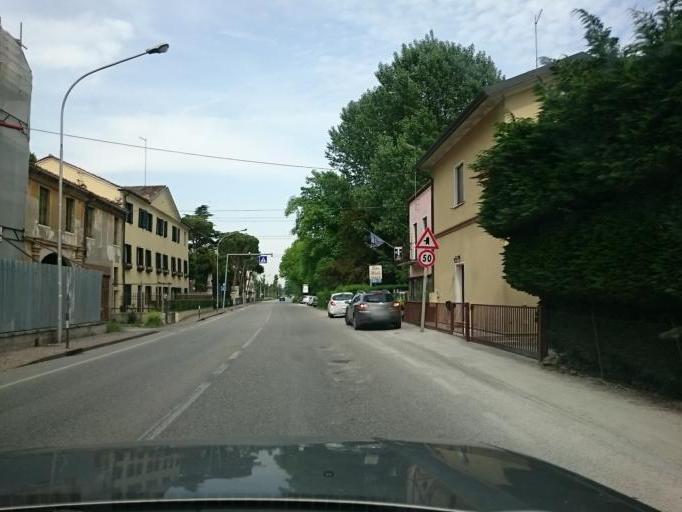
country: IT
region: Veneto
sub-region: Provincia di Venezia
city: Mira Taglio
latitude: 45.4272
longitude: 12.1043
